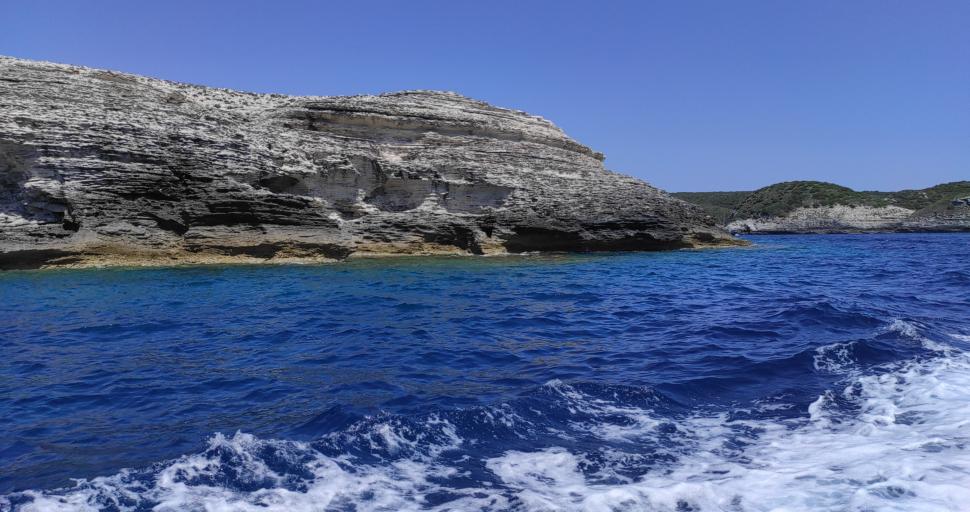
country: FR
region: Corsica
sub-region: Departement de la Corse-du-Sud
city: Bonifacio
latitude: 41.3927
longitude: 9.1289
